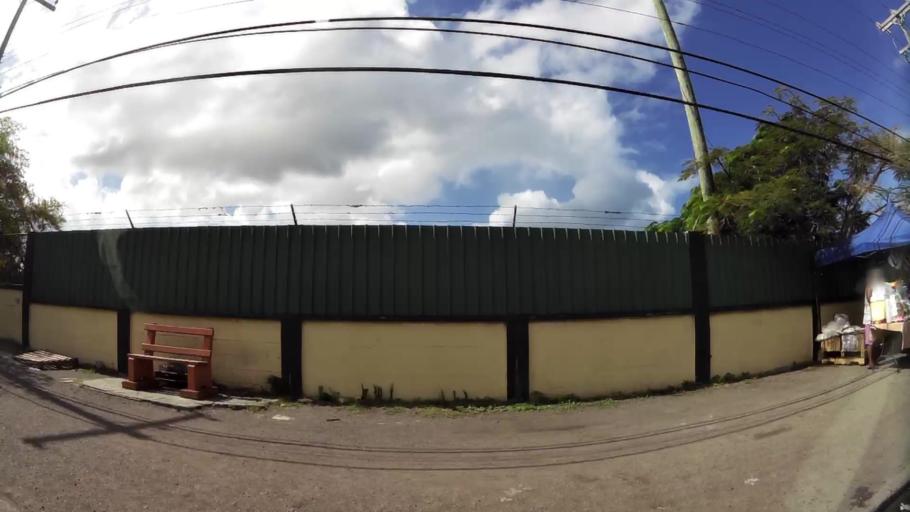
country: AG
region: Saint John
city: Saint John's
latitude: 17.1157
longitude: -61.8443
